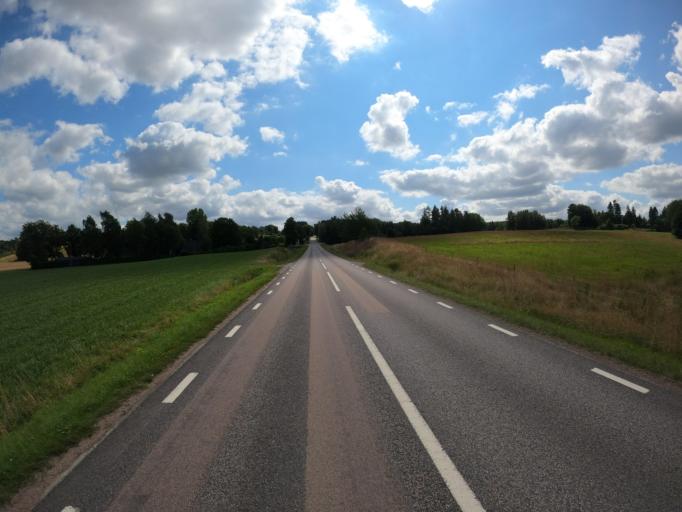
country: SE
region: Skane
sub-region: Lunds Kommun
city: Veberod
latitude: 55.5911
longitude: 13.4948
